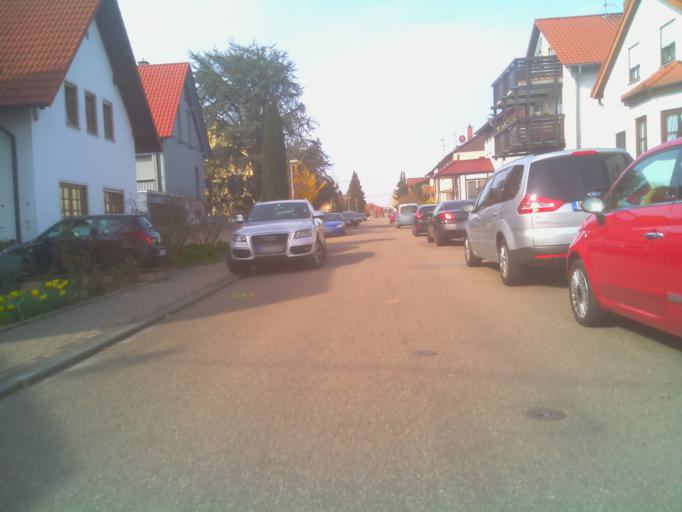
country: DE
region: Baden-Wuerttemberg
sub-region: Karlsruhe Region
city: Schriesheim
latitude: 49.4686
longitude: 8.6635
